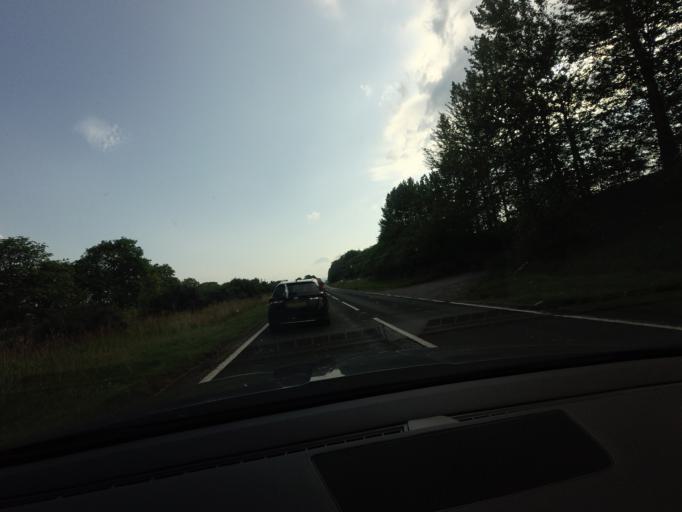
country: GB
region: Scotland
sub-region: Highland
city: Evanton
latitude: 57.6436
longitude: -4.3448
